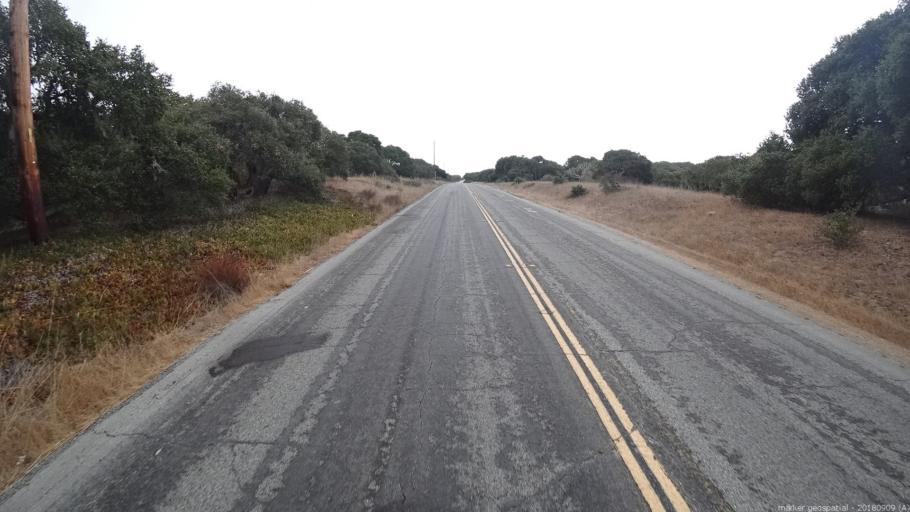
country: US
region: California
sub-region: Monterey County
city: Marina
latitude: 36.6555
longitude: -121.7516
